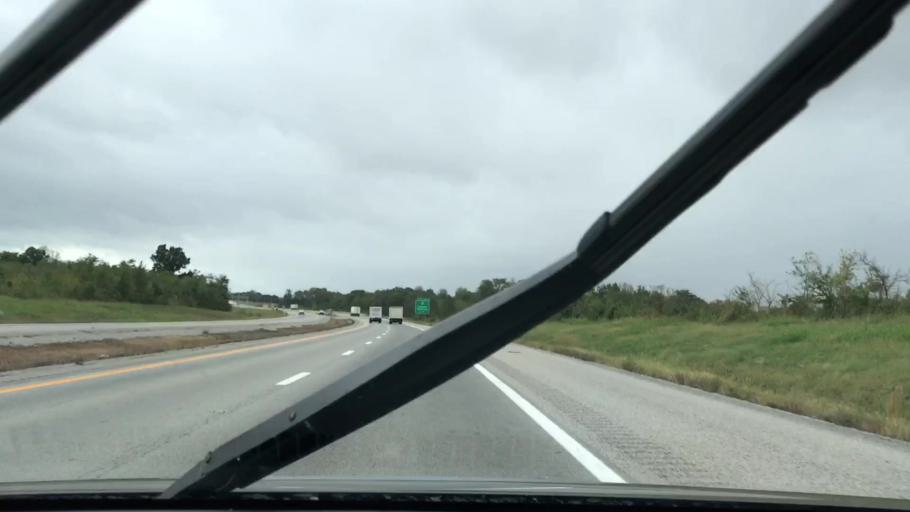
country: US
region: Kentucky
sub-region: Christian County
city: Hopkinsville
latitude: 36.7577
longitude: -87.5055
